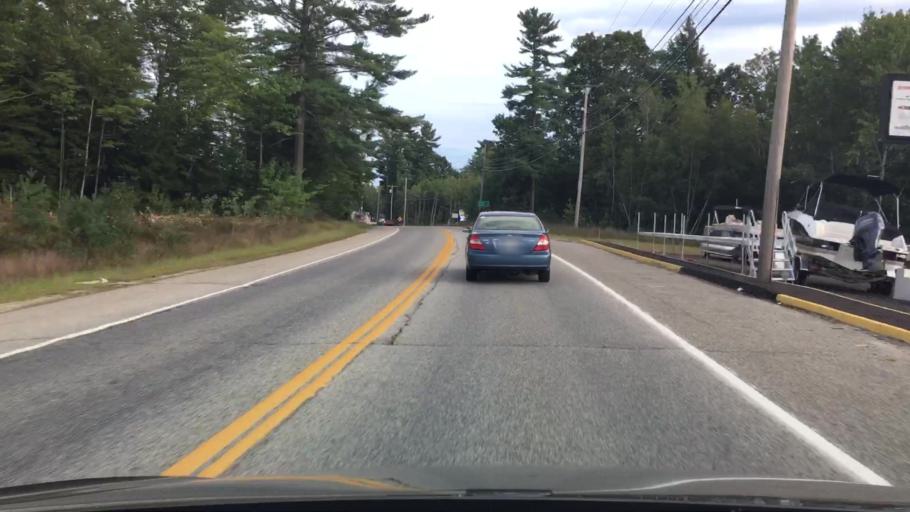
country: US
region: Maine
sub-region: Cumberland County
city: Bridgton
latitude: 44.0354
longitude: -70.6992
